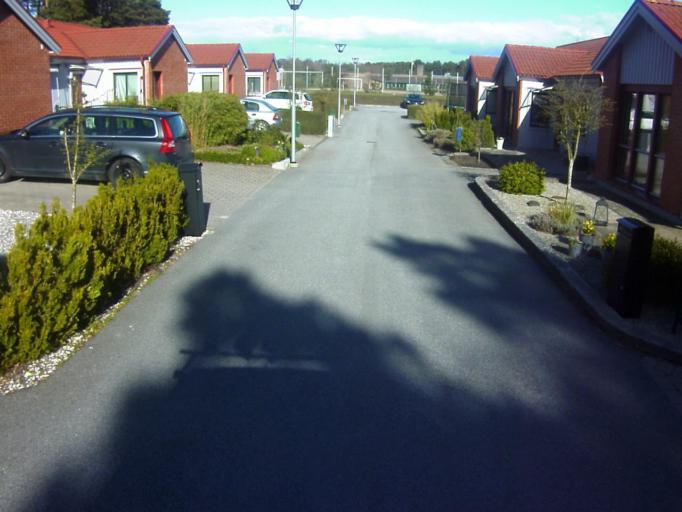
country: SE
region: Skane
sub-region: Kavlinge Kommun
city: Hofterup
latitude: 55.8081
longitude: 12.9739
